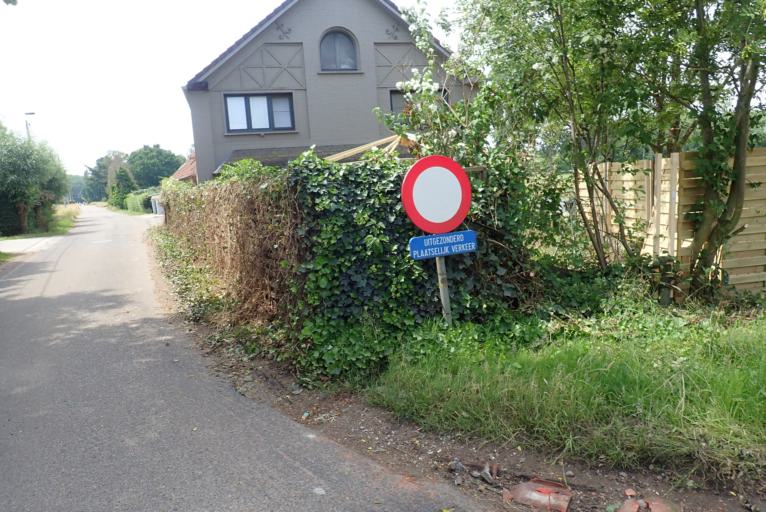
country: BE
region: Flanders
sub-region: Provincie Antwerpen
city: Zandhoven
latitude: 51.2118
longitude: 4.6886
